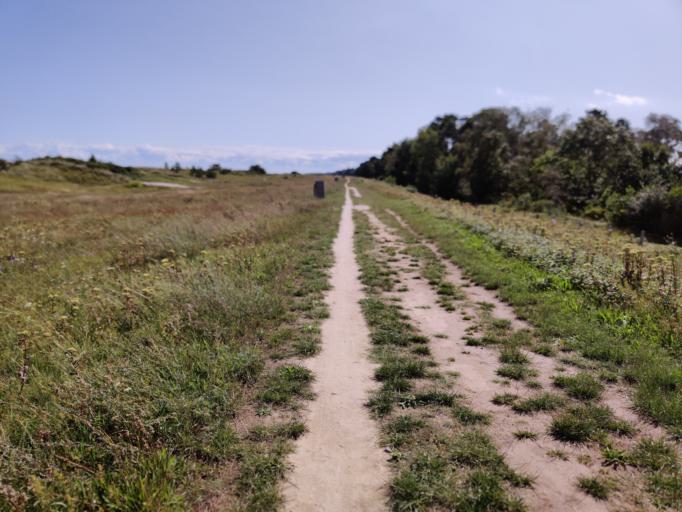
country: DK
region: Zealand
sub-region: Guldborgsund Kommune
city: Nykobing Falster
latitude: 54.6574
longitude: 11.9596
